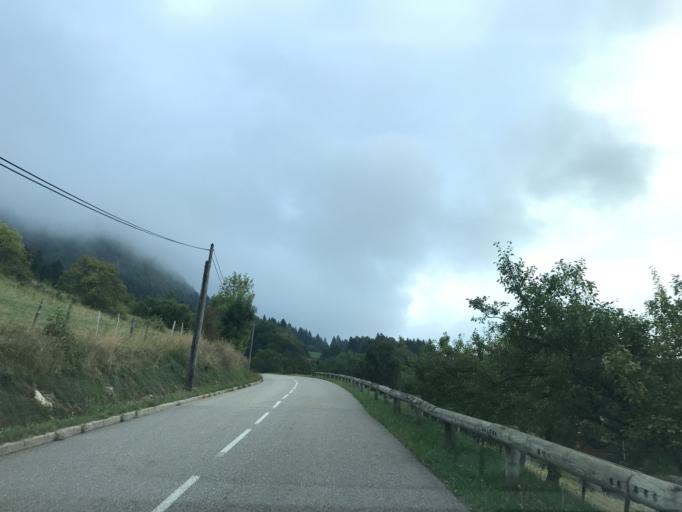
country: FR
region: Rhone-Alpes
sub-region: Departement de la Haute-Savoie
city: Talloires
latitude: 45.8291
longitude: 6.2379
